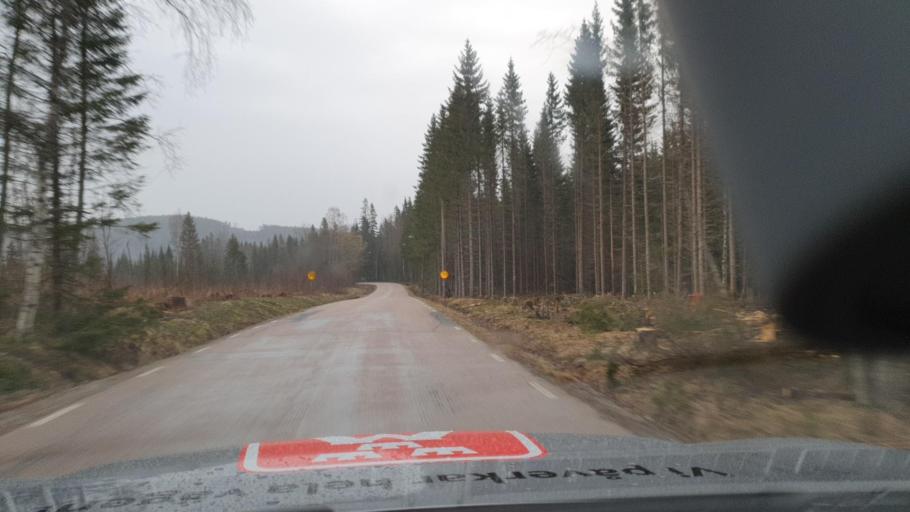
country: SE
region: Vaesternorrland
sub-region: OErnskoeldsviks Kommun
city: Bjasta
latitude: 63.2044
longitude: 18.4180
